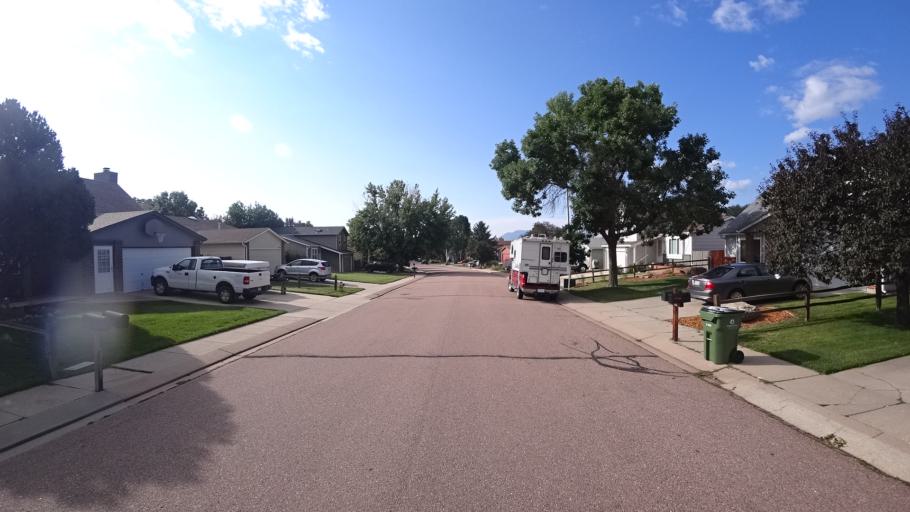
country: US
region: Colorado
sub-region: El Paso County
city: Air Force Academy
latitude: 38.9156
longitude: -104.8606
